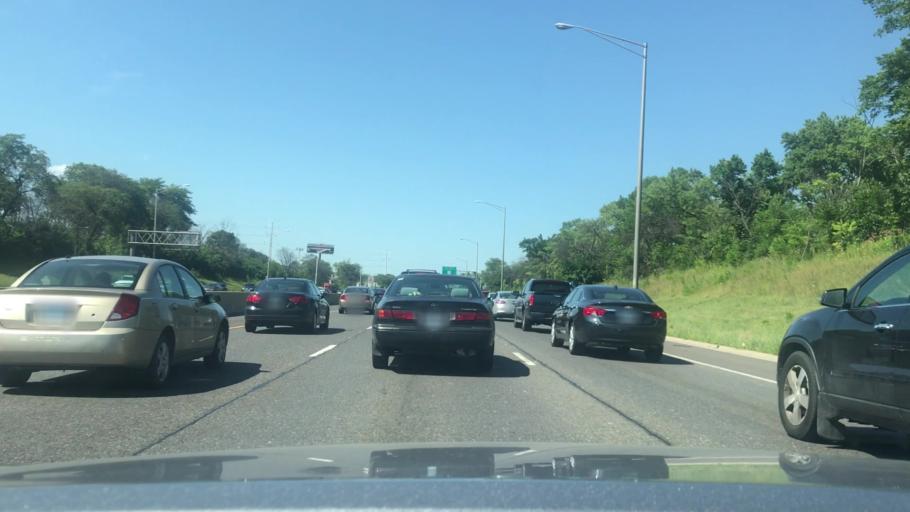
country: US
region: Illinois
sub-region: Cook County
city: Calumet Park
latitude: 41.7076
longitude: -87.6529
